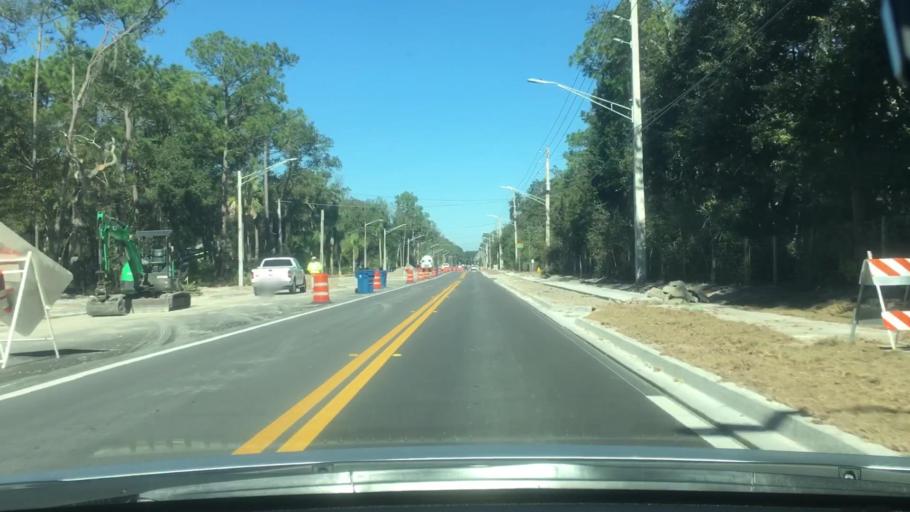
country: US
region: Florida
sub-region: Duval County
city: Atlantic Beach
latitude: 30.3411
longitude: -81.4617
